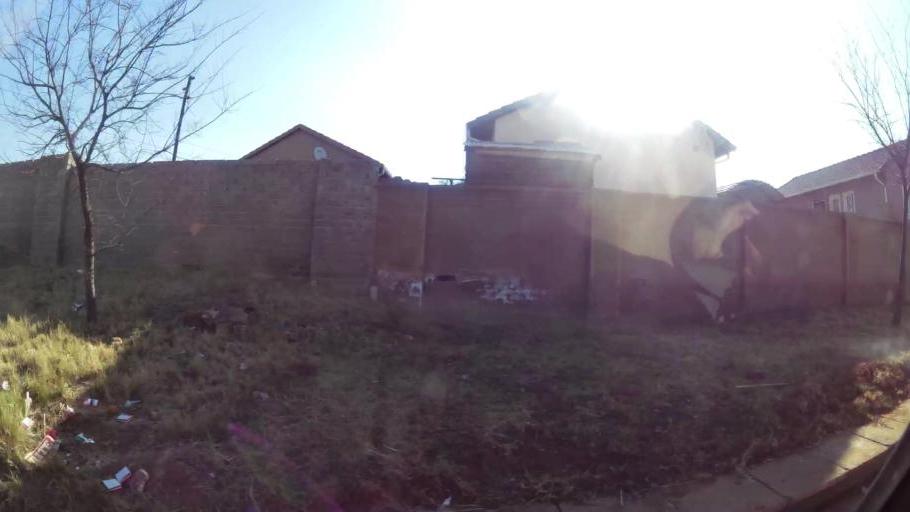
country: ZA
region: Gauteng
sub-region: West Rand District Municipality
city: Muldersdriseloop
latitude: -26.0369
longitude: 27.9146
